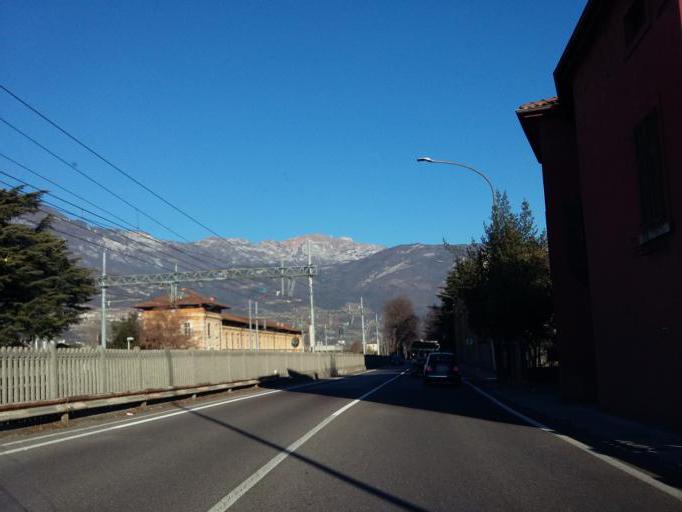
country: IT
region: Trentino-Alto Adige
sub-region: Provincia di Trento
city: Rovereto
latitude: 45.8941
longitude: 11.0343
